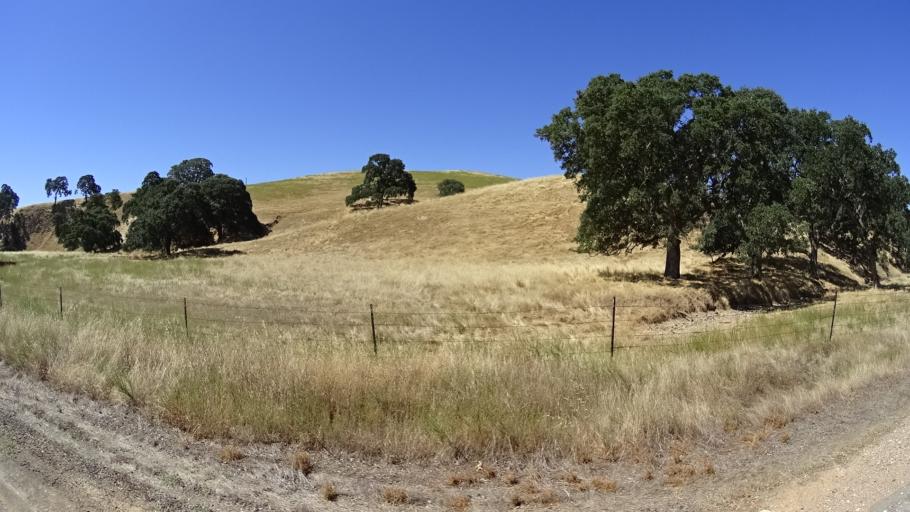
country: US
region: California
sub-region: Calaveras County
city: Rancho Calaveras
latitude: 38.0246
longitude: -120.8410
